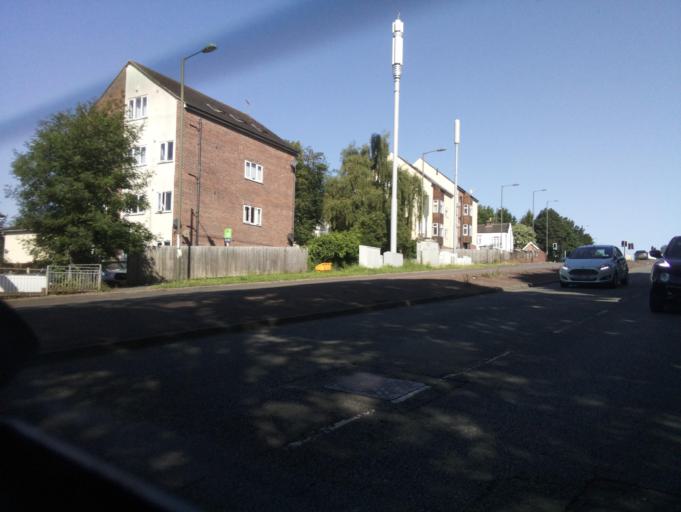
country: GB
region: England
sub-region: Derby
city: Derby
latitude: 52.9070
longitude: -1.5002
